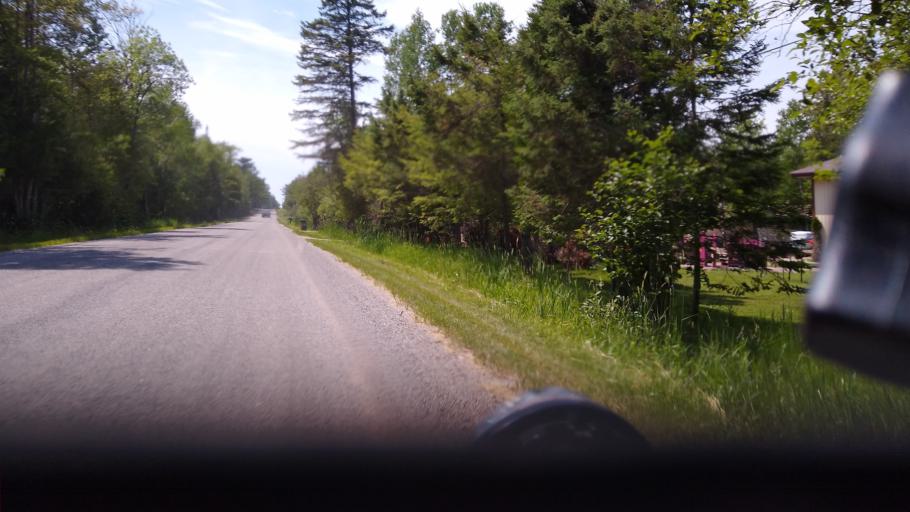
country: US
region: Michigan
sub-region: Delta County
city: Escanaba
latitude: 45.7102
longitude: -87.1452
